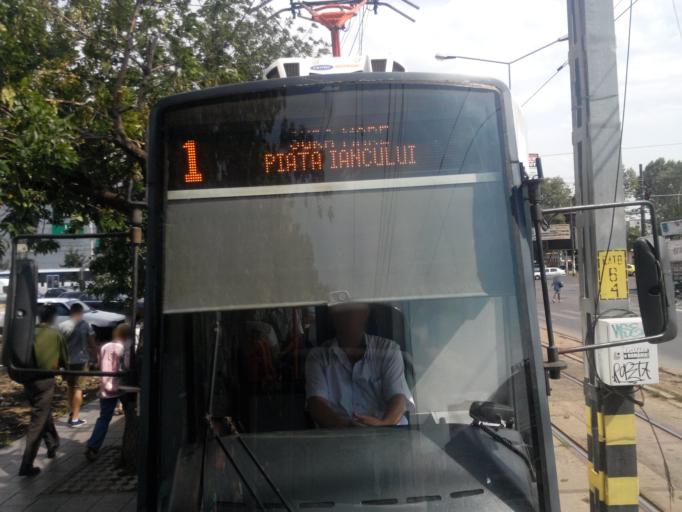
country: RO
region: Bucuresti
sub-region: Municipiul Bucuresti
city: Bucuresti
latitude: 44.4160
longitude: 26.0781
